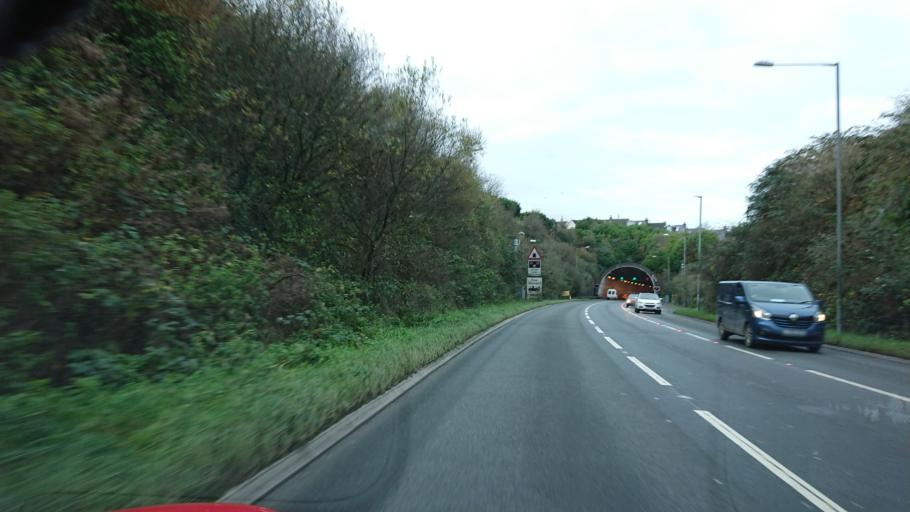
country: GB
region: England
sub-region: Cornwall
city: Saltash
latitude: 50.4092
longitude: -4.2111
